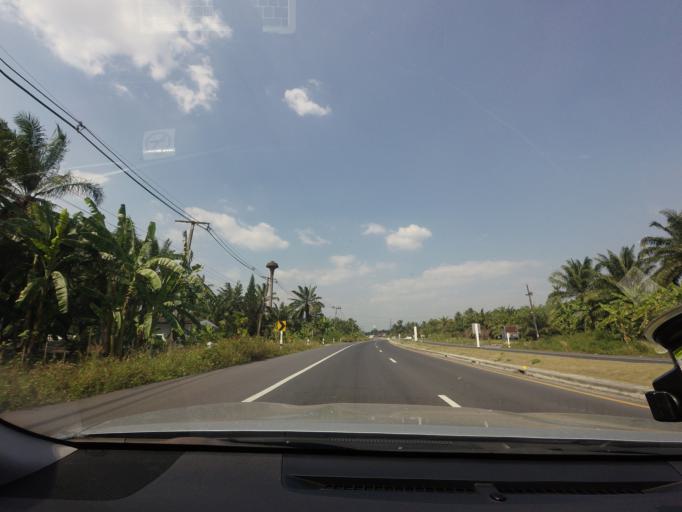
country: TH
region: Phangnga
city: Thap Put
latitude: 8.5545
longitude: 98.7318
